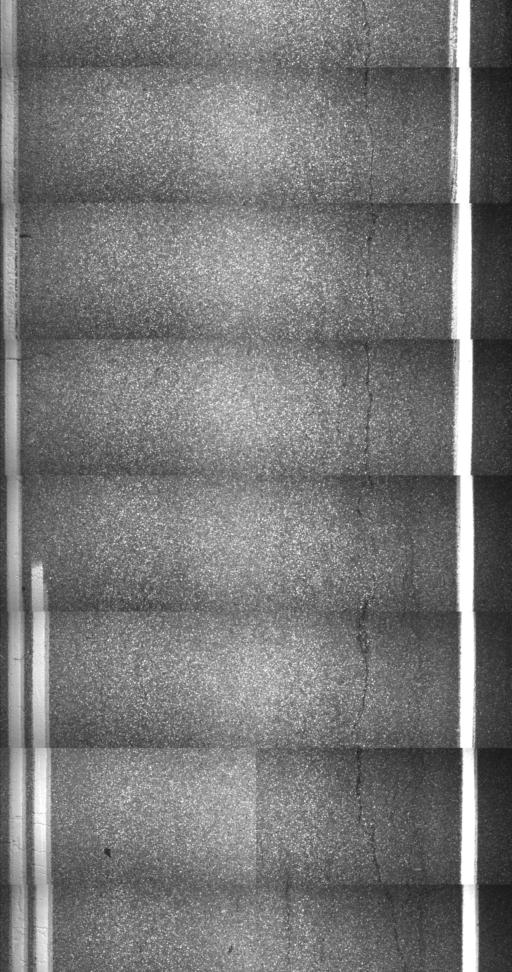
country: US
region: Vermont
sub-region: Chittenden County
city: Williston
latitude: 44.4506
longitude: -73.0179
